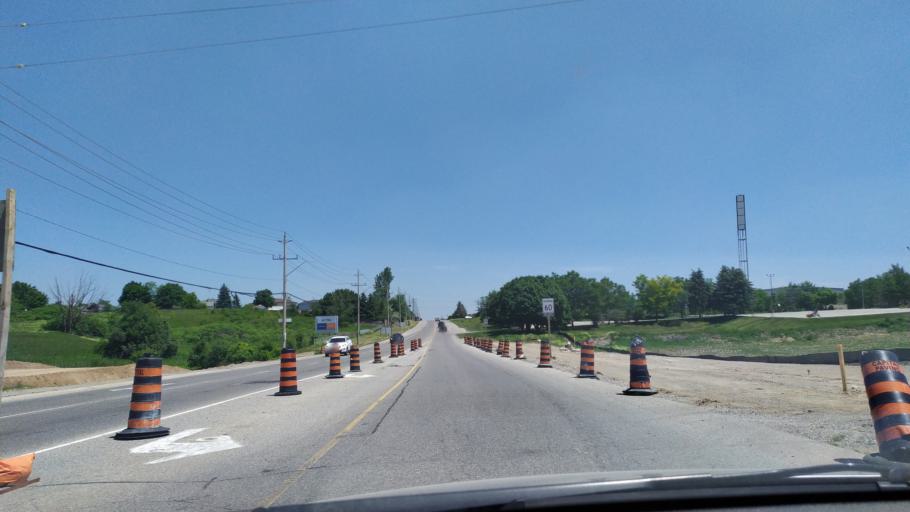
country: CA
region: Ontario
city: Kitchener
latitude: 43.4023
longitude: -80.4972
